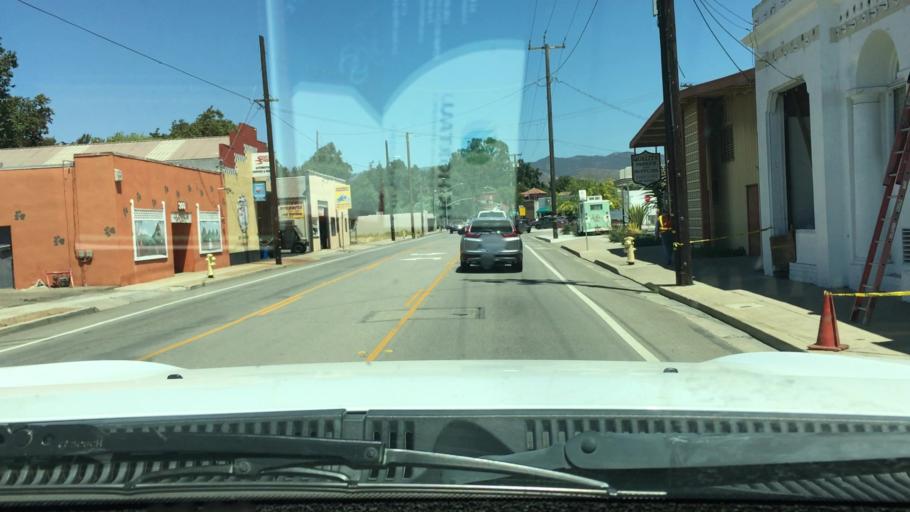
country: US
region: California
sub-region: San Luis Obispo County
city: San Luis Obispo
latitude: 35.2727
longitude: -120.6697
